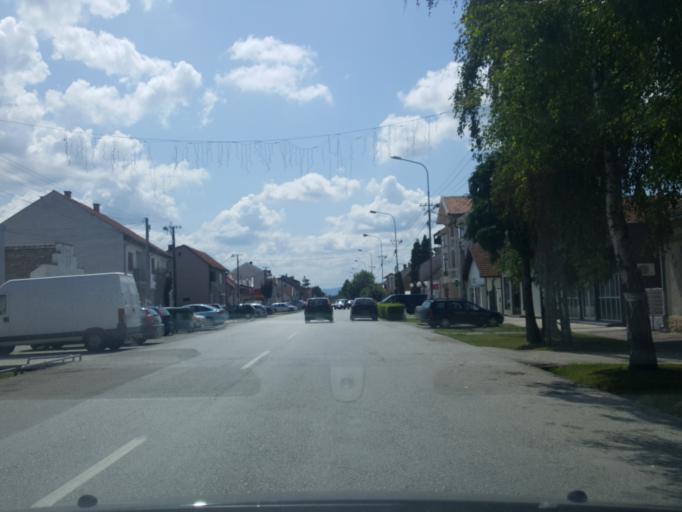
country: RS
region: Central Serbia
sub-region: Macvanski Okrug
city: Bogatic
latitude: 44.8337
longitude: 19.4795
